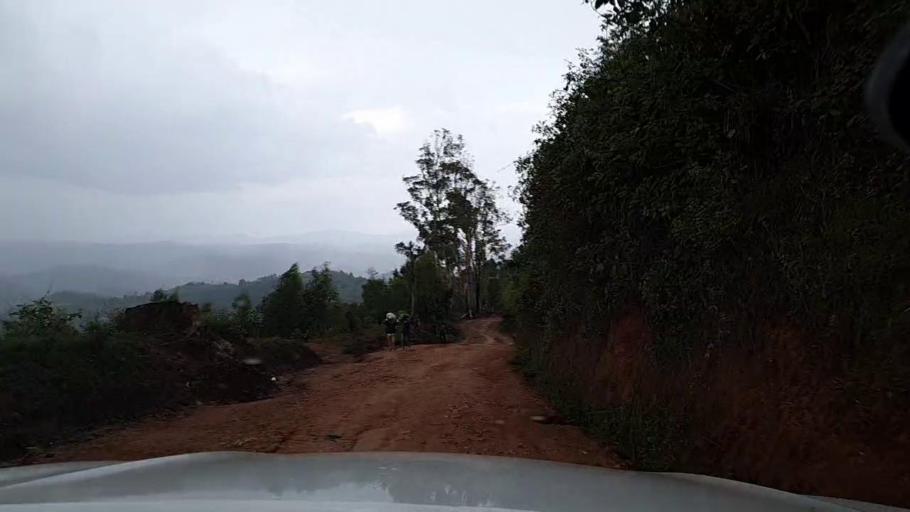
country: BI
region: Kayanza
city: Kayanza
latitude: -2.7864
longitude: 29.5312
